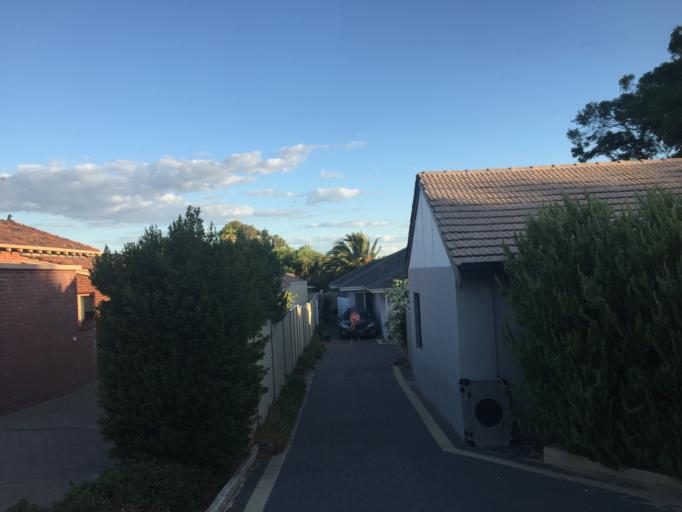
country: AU
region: Western Australia
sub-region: Belmont
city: Rivervale
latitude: -31.9552
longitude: 115.9159
